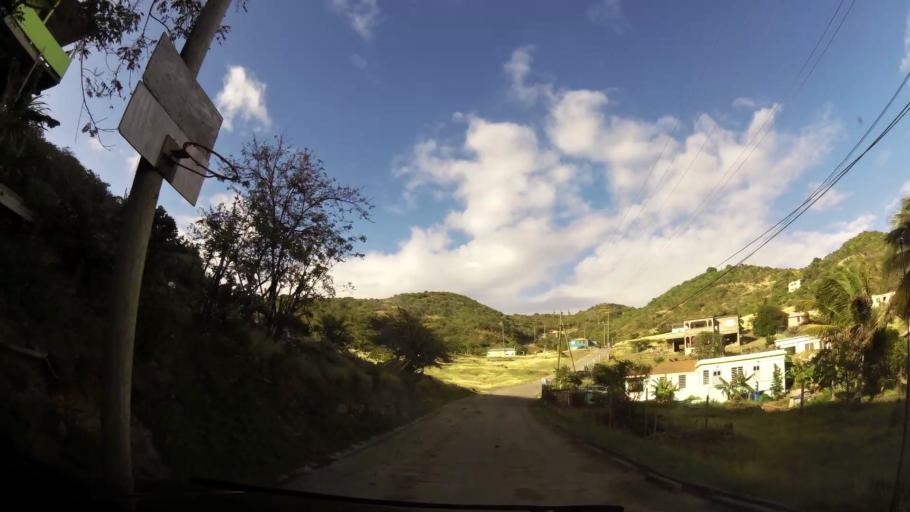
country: MS
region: Saint Peter
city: Brades
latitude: 16.7989
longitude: -62.1947
